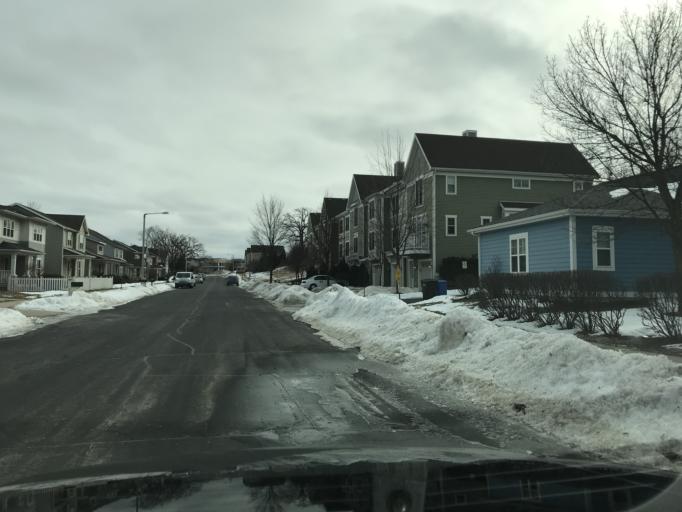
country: US
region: Wisconsin
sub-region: Dane County
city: Monona
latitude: 43.0880
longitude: -89.2788
